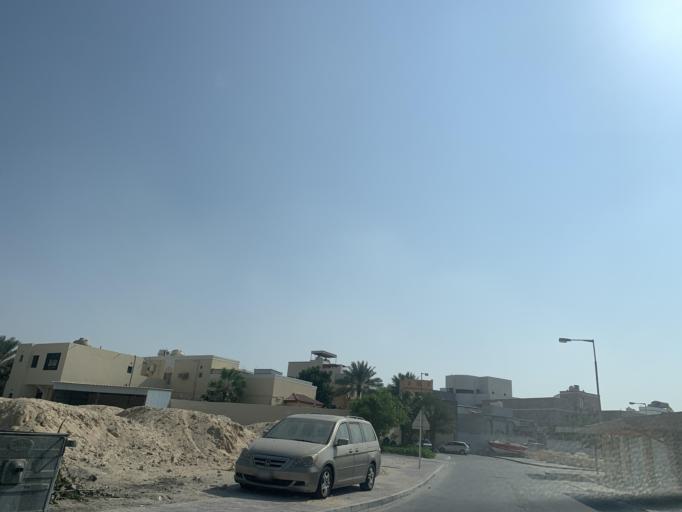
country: BH
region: Central Governorate
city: Madinat Hamad
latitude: 26.1194
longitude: 50.4907
